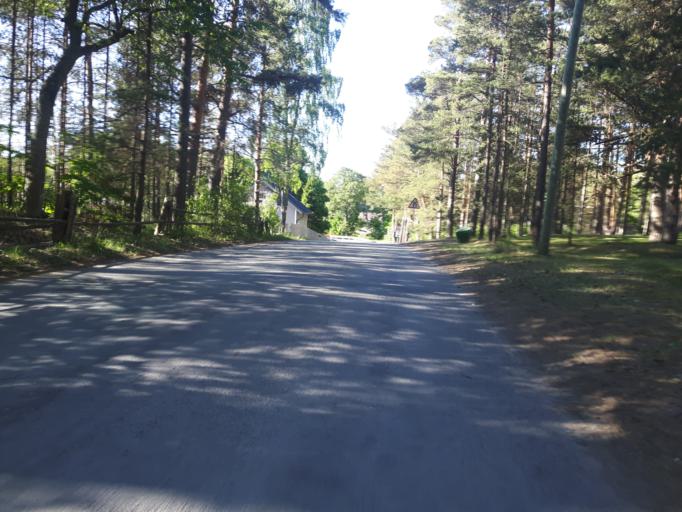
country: EE
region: Harju
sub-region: Loksa linn
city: Loksa
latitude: 59.5775
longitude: 25.9708
